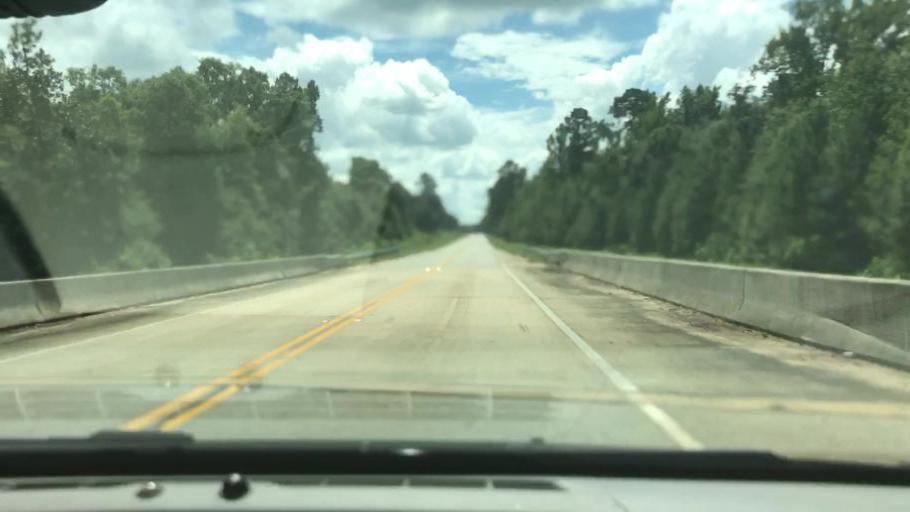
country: US
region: Georgia
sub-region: Stewart County
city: Lumpkin
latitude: 32.1223
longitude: -85.0357
